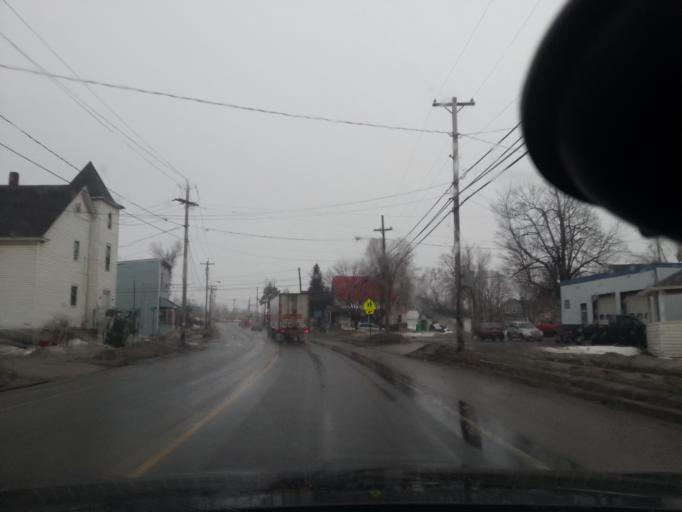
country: US
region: New York
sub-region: St. Lawrence County
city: Gouverneur
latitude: 44.3287
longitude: -75.4777
